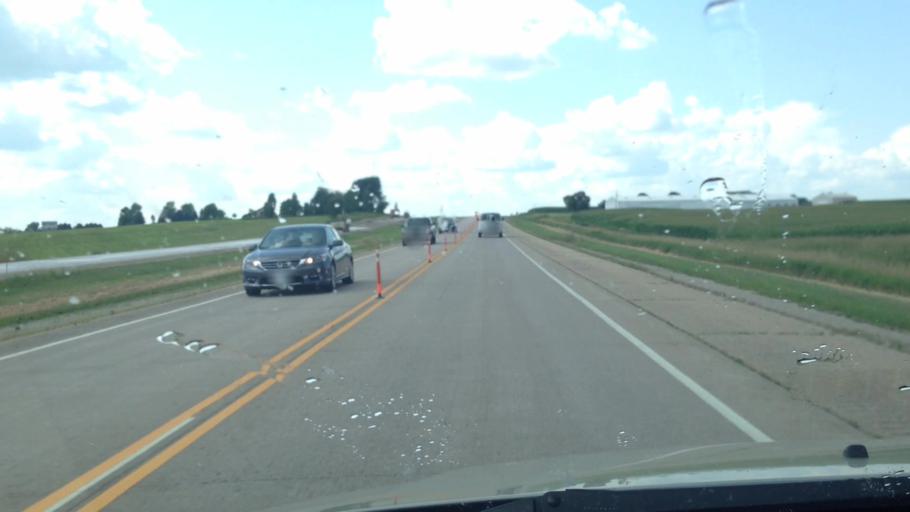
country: US
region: Wisconsin
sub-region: Shawano County
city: Bonduel
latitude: 44.6968
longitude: -88.3500
